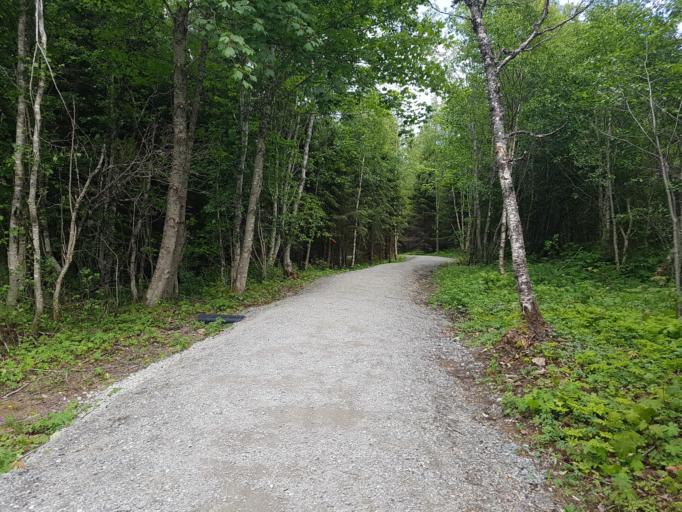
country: NO
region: Sor-Trondelag
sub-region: Trondheim
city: Trondheim
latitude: 63.4160
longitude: 10.3240
